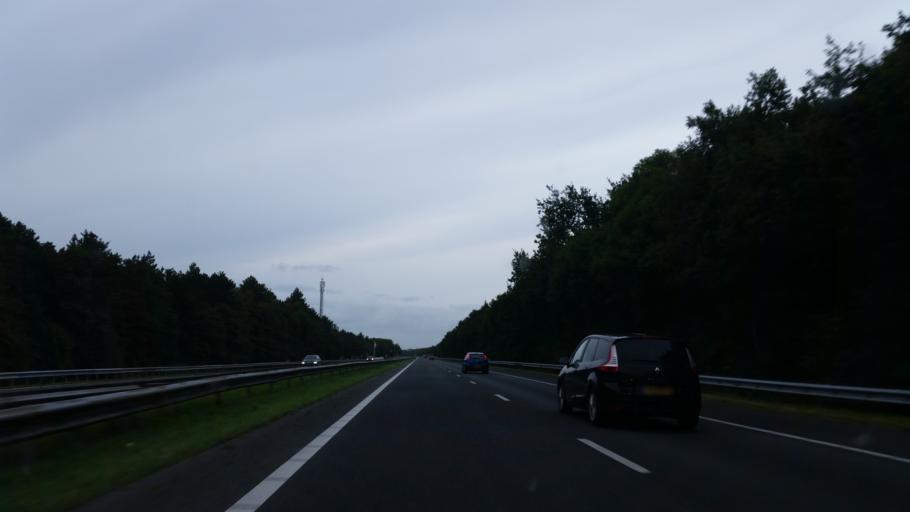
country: NL
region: North Holland
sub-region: Gemeente Hollands Kroon
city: Den Oever
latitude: 52.9037
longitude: 5.0295
